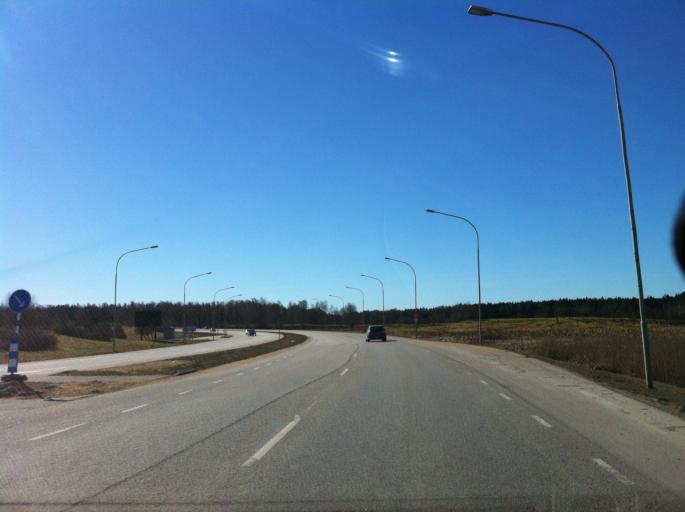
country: SE
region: Vaestra Goetaland
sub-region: Vanersborgs Kommun
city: Vargon
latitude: 58.3535
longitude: 12.4022
